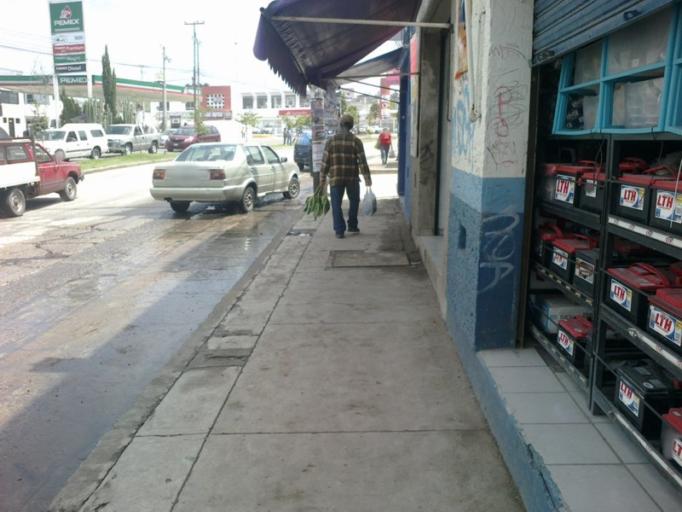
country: MX
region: Queretaro
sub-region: Queretaro
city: Sergio Villasenor
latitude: 20.6293
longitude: -100.4065
